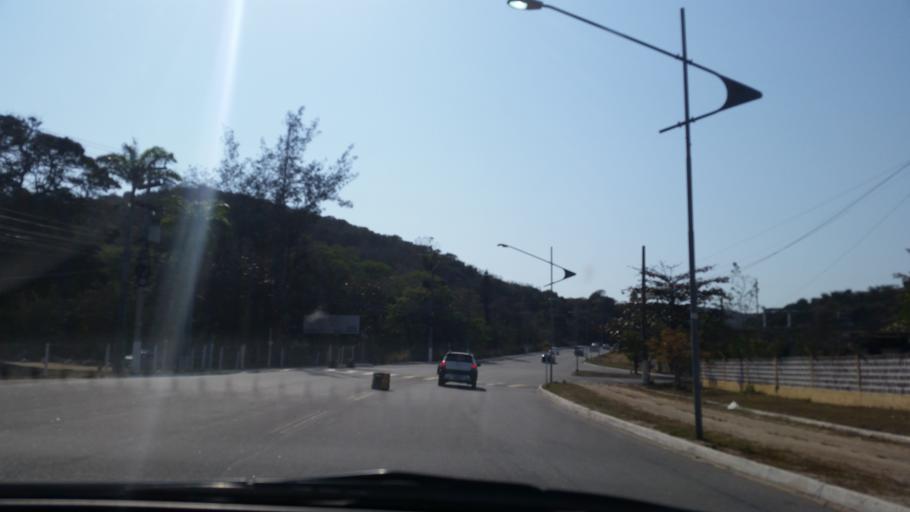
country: BR
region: Rio de Janeiro
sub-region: Arraial Do Cabo
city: Arraial do Cabo
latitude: -22.9552
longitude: -42.0311
